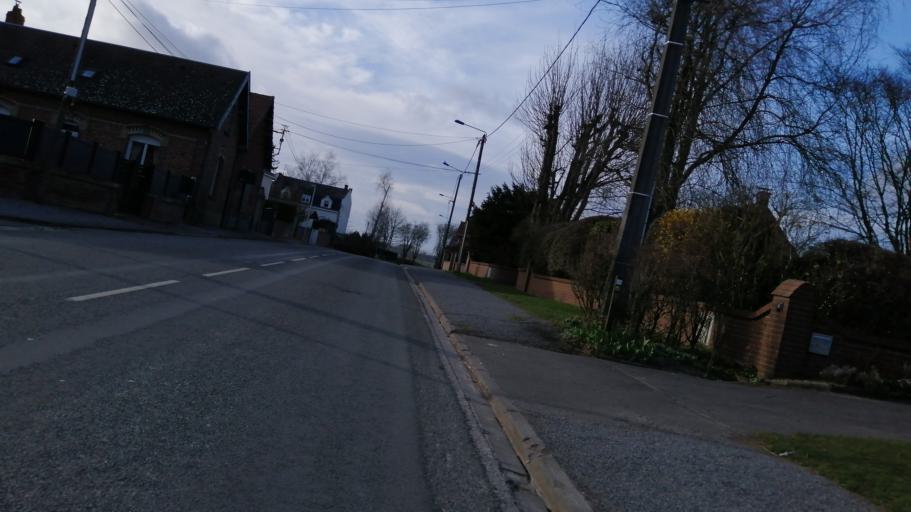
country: FR
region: Nord-Pas-de-Calais
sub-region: Departement du Pas-de-Calais
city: Beaurains
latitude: 50.2460
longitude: 2.8160
